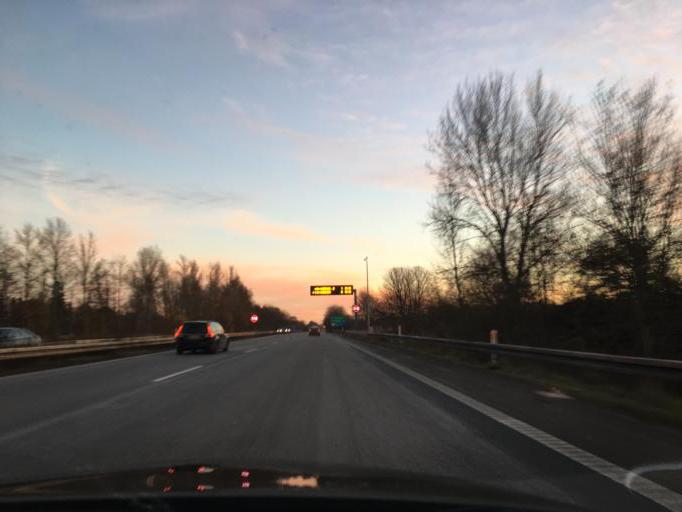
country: DK
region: Capital Region
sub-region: Fredensborg Kommune
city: Kokkedal
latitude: 55.9026
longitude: 12.4731
